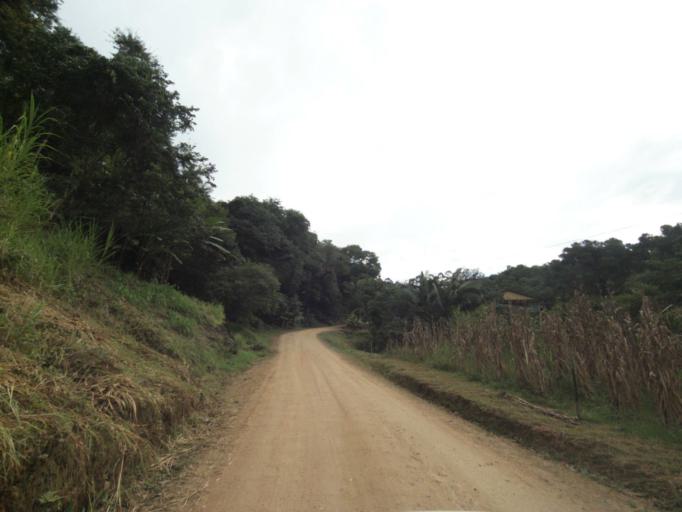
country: BR
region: Santa Catarina
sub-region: Pomerode
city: Pomerode
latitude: -26.7323
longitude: -49.1926
